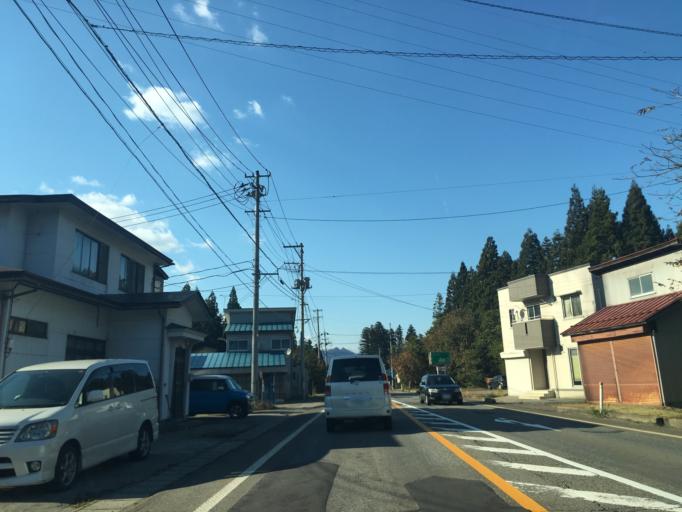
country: JP
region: Fukushima
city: Kitakata
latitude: 37.5768
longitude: 139.6613
